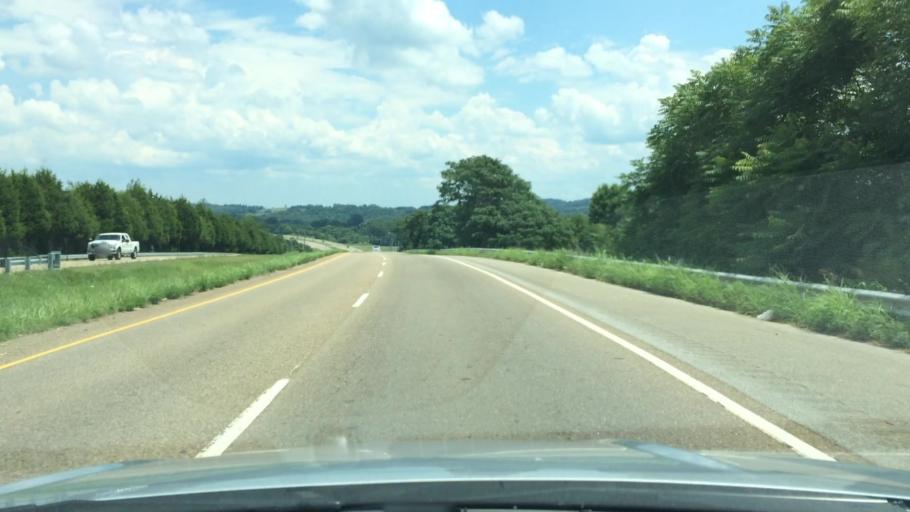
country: US
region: Tennessee
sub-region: Hamblen County
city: Morristown
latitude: 36.1702
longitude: -83.3850
